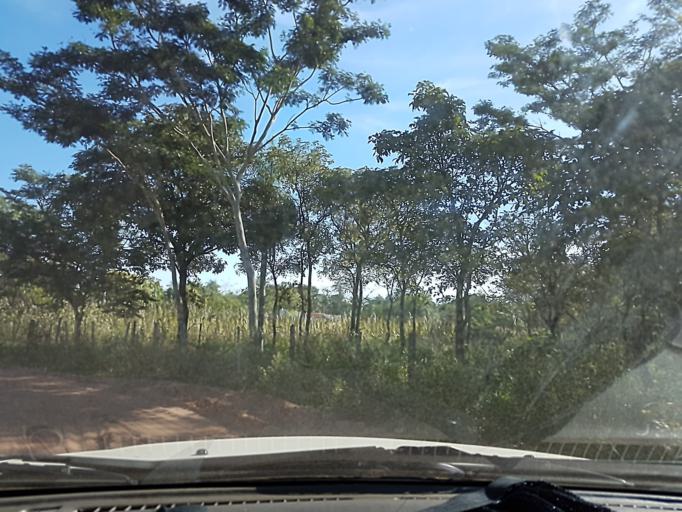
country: PY
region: Cordillera
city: Arroyos y Esteros
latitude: -24.9778
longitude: -57.1955
